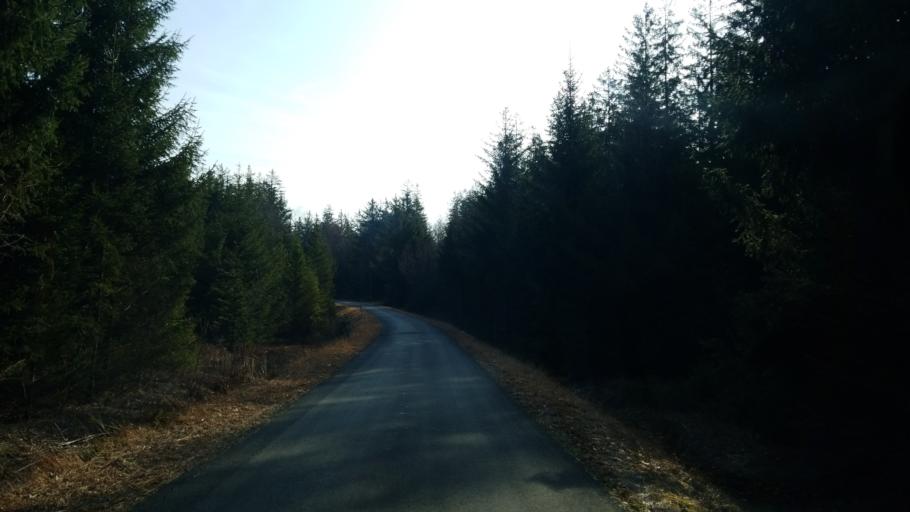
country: US
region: Pennsylvania
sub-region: Clearfield County
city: Shiloh
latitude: 41.2281
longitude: -78.2149
